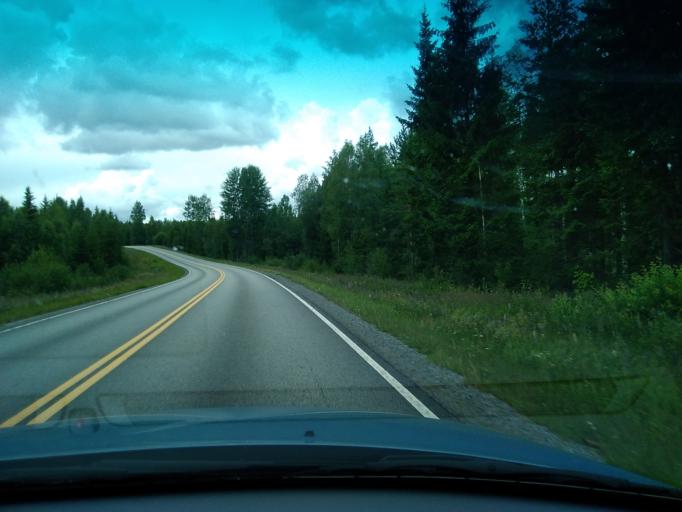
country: FI
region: Central Finland
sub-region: Saarijaervi-Viitasaari
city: Pylkoenmaeki
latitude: 62.6499
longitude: 24.9940
